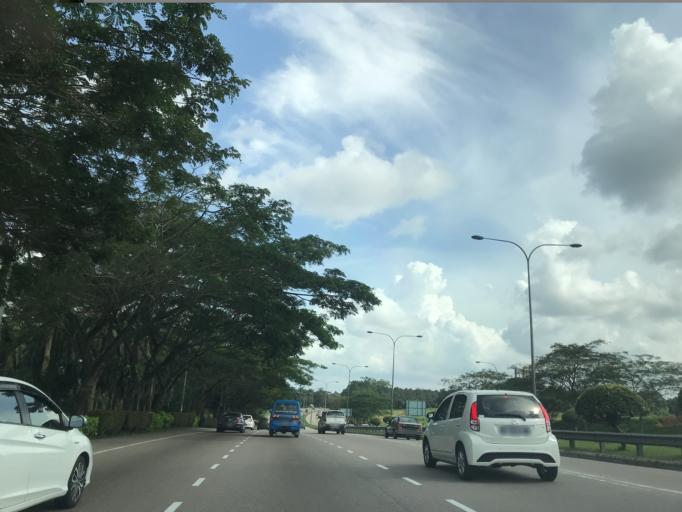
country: MY
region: Johor
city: Taman Senai
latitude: 1.5831
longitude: 103.6519
